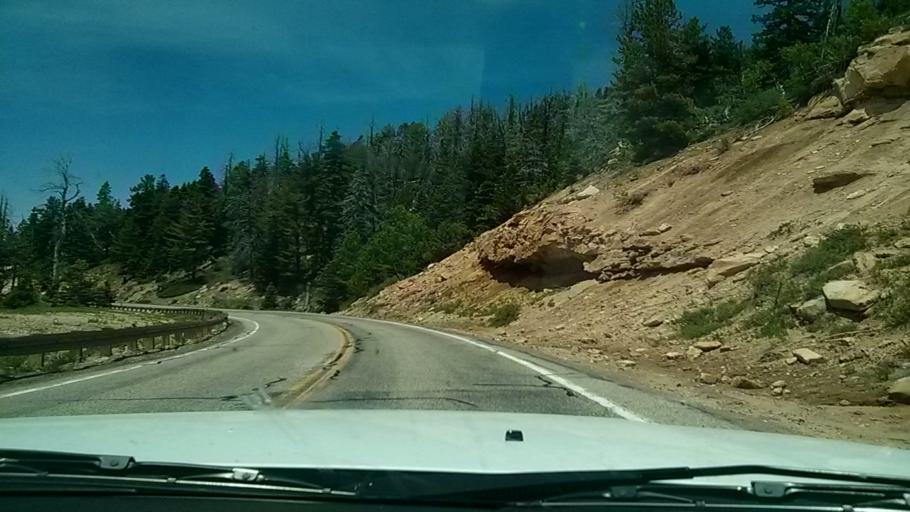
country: US
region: Utah
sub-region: Iron County
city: Cedar City
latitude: 37.5767
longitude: -112.8641
